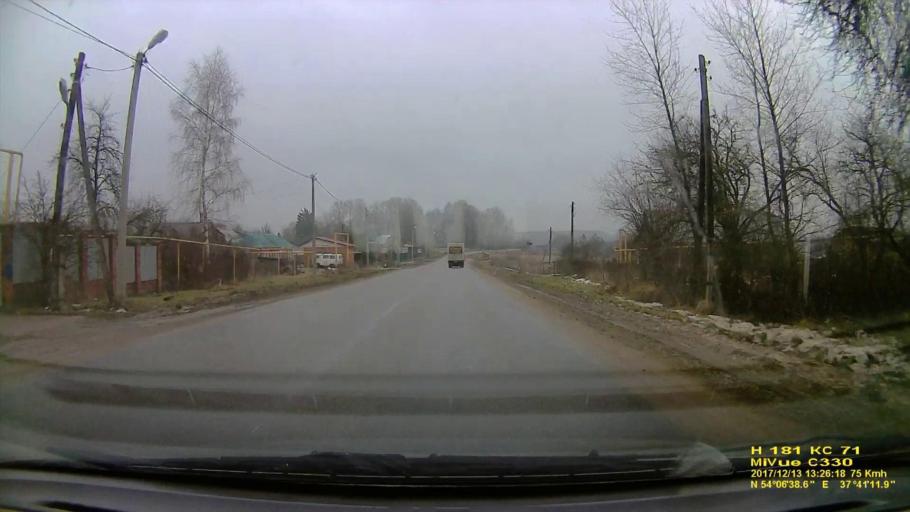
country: RU
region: Tula
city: Skuratovskiy
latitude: 54.1107
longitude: 37.6868
